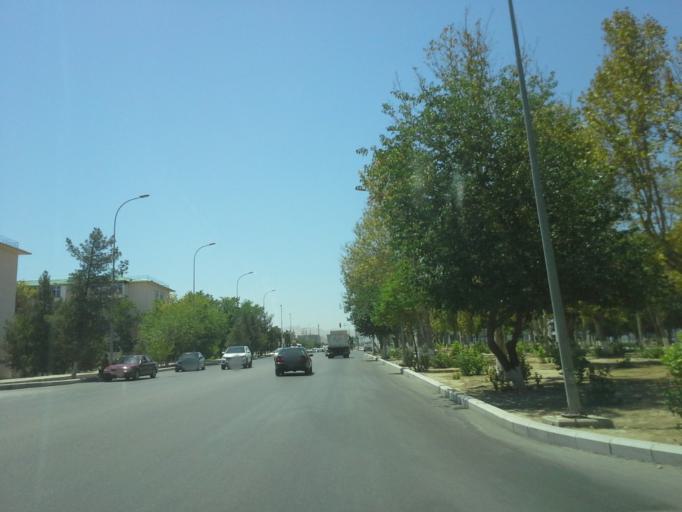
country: TM
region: Ahal
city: Ashgabat
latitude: 37.9120
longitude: 58.4058
